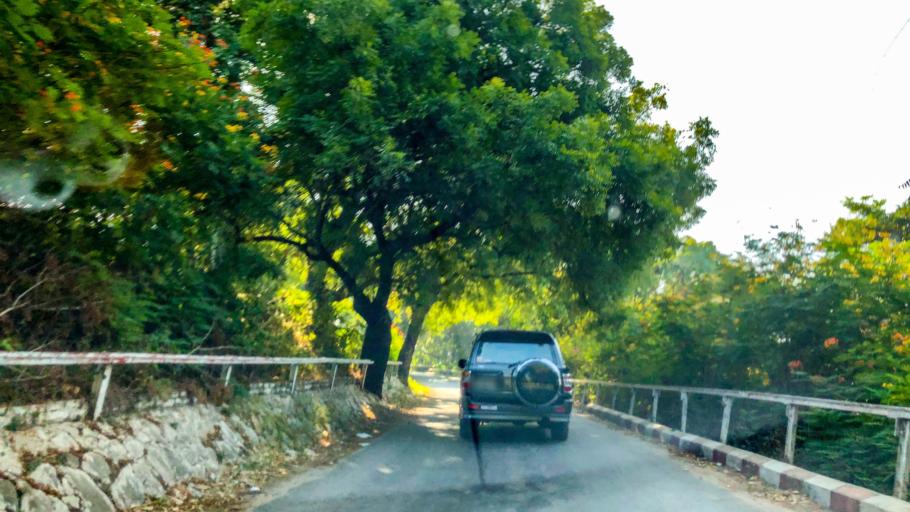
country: MM
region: Sagain
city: Sagaing
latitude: 21.8767
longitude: 95.9865
